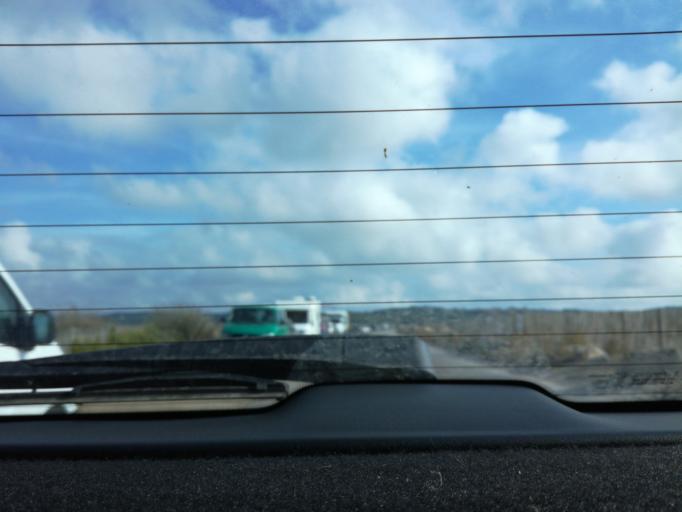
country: FR
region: Provence-Alpes-Cote d'Azur
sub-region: Departement du Var
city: Hyeres
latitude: 43.0571
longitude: 6.1335
